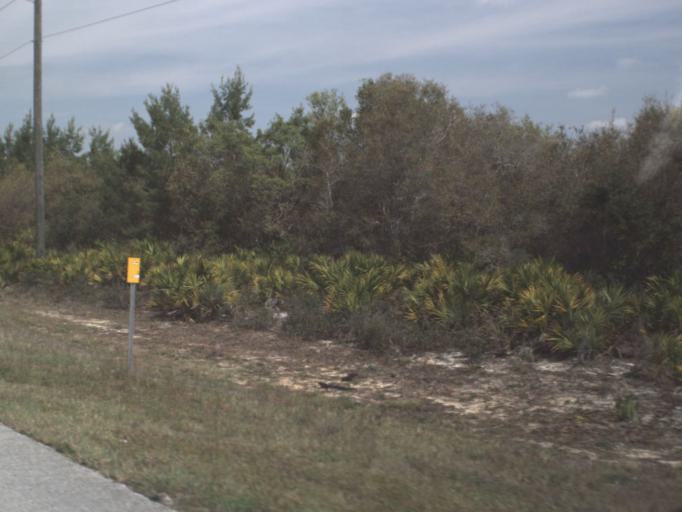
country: US
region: Florida
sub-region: Putnam County
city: Crescent City
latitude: 29.3248
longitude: -81.7042
